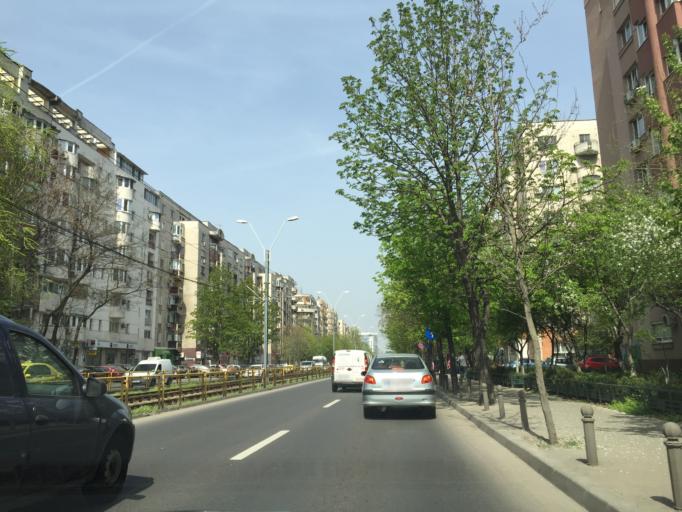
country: RO
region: Ilfov
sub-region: Comuna Chiajna
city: Rosu
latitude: 44.4371
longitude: 26.0353
